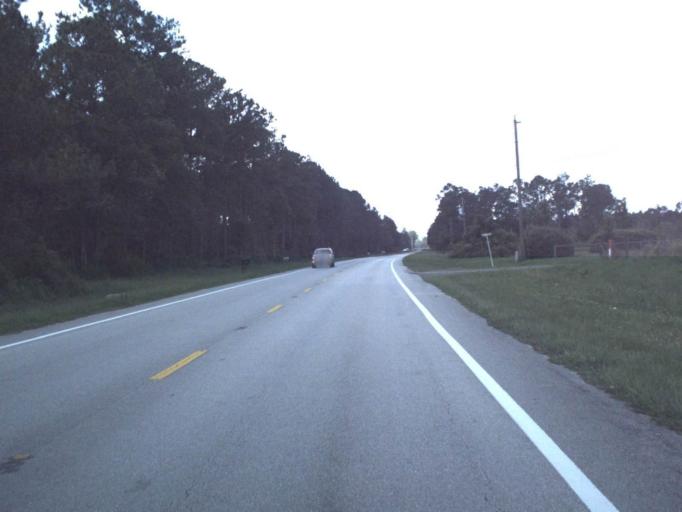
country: US
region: Florida
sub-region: Bradford County
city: Starke
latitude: 29.9863
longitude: -82.1273
